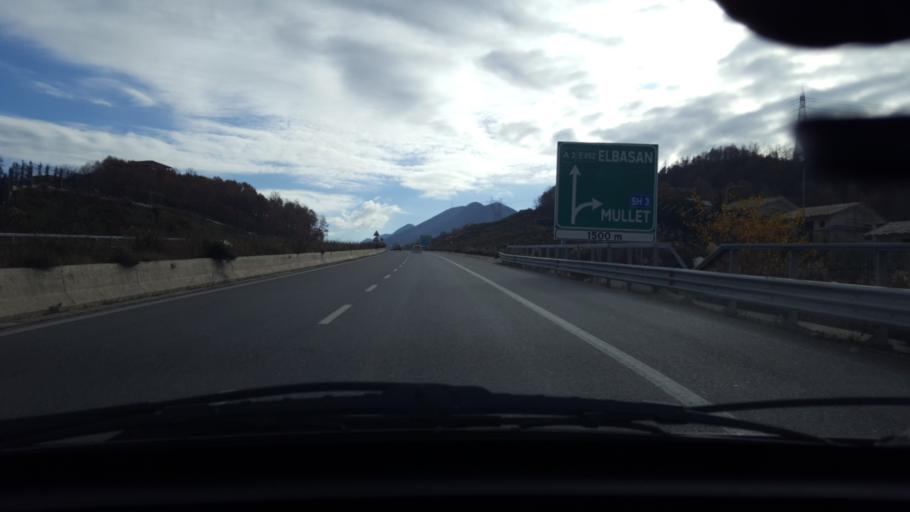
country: AL
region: Tirane
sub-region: Rrethi i Tiranes
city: Petrele
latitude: 41.2728
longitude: 19.8589
